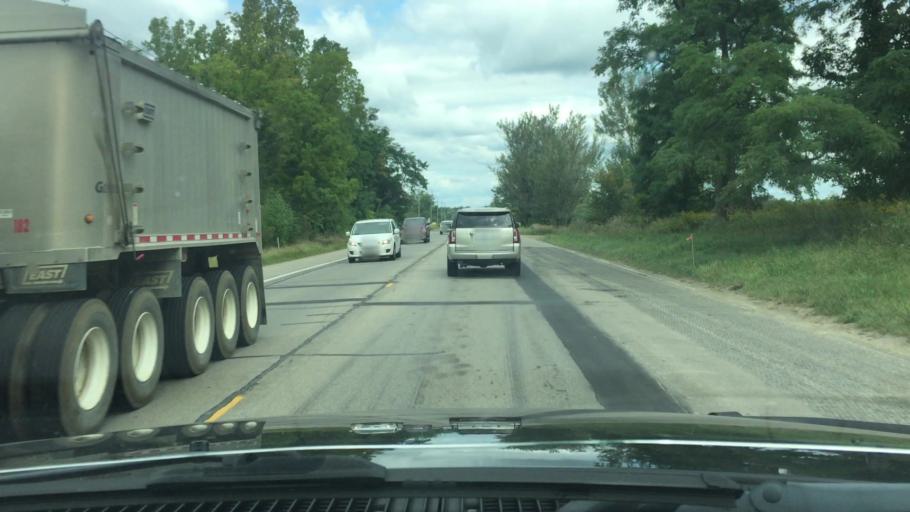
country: US
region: Michigan
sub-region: Lapeer County
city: Almont
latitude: 42.8954
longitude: -83.0437
